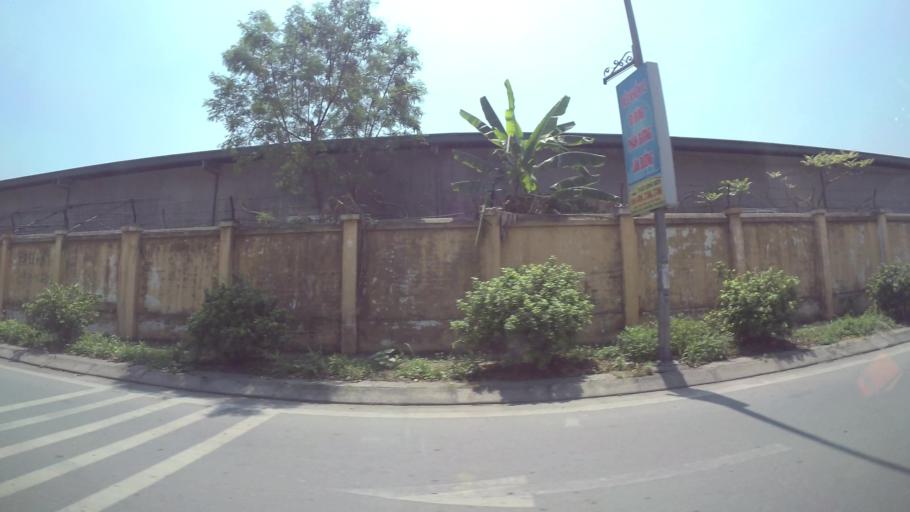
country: VN
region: Ha Noi
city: Hoan Kiem
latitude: 21.0510
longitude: 105.8901
